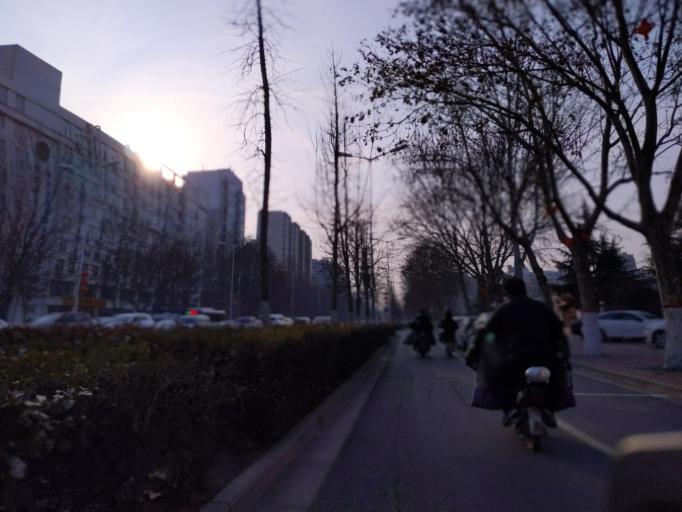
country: CN
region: Henan Sheng
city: Puyang
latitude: 35.7813
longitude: 115.0188
